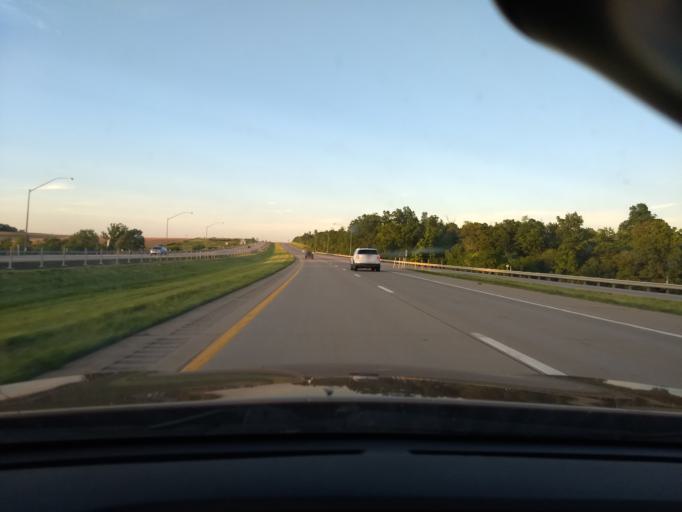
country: US
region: Pennsylvania
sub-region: Centre County
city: Houserville
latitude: 40.8479
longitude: -77.8083
